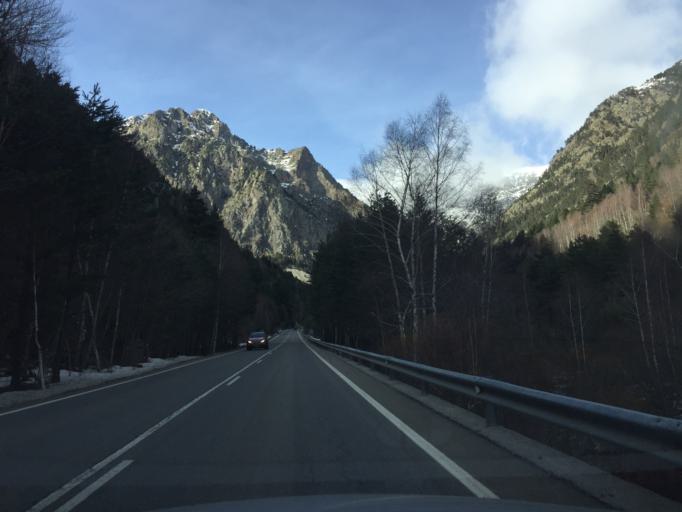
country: ES
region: Aragon
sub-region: Provincia de Huesca
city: Bielsa
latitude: 42.6928
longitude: 0.2041
